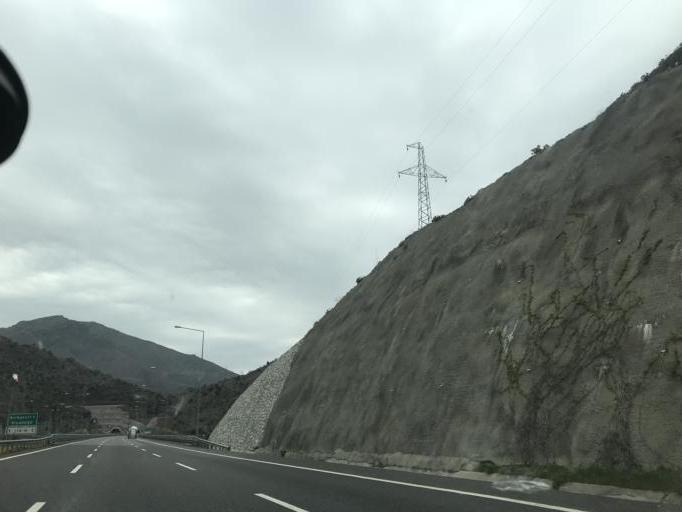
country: TR
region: Nigde
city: Ciftehan
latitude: 37.5529
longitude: 34.7752
